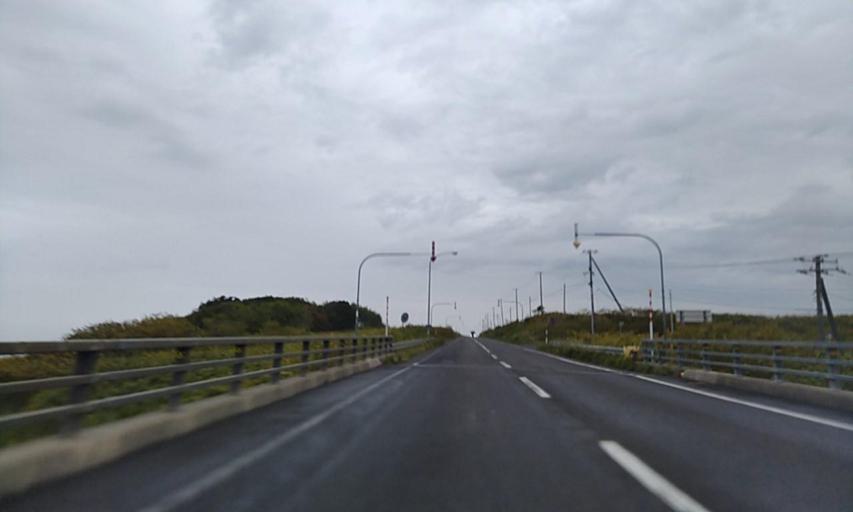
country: JP
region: Hokkaido
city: Mombetsu
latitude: 44.5401
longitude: 143.0219
